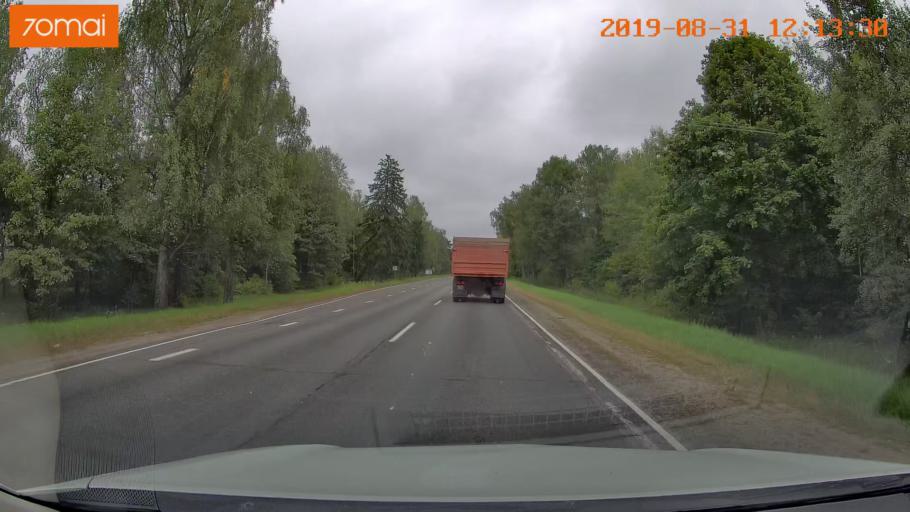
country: BY
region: Mogilev
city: Klimavichy
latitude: 53.7093
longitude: 31.8735
